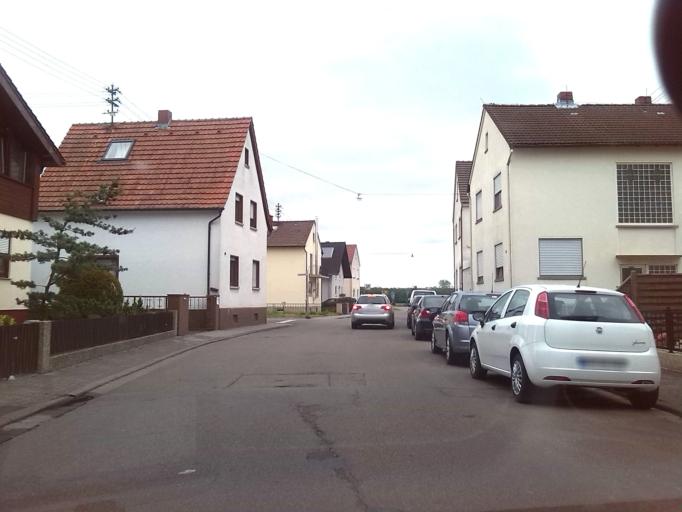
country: DE
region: Rheinland-Pfalz
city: Bohl-Iggelheim
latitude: 49.3675
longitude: 8.3124
